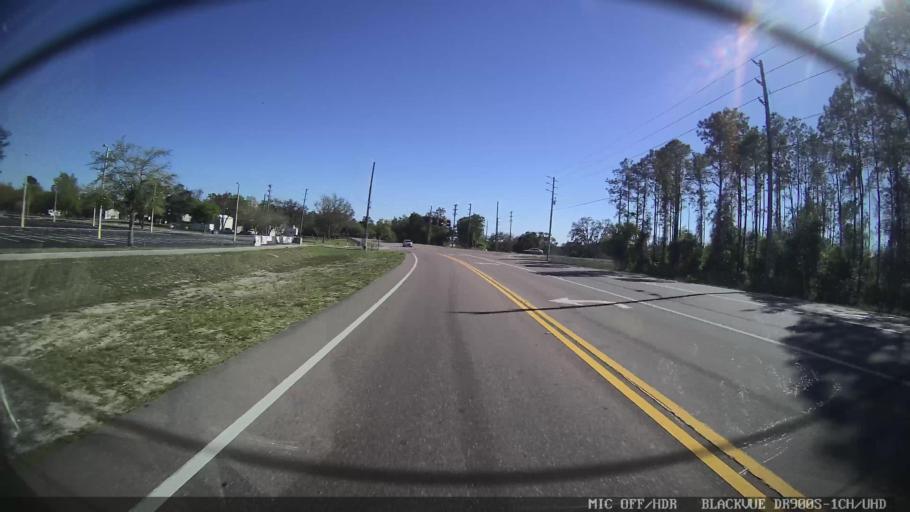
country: US
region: Florida
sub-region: Pasco County
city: Shady Hills
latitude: 28.3767
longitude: -82.5517
